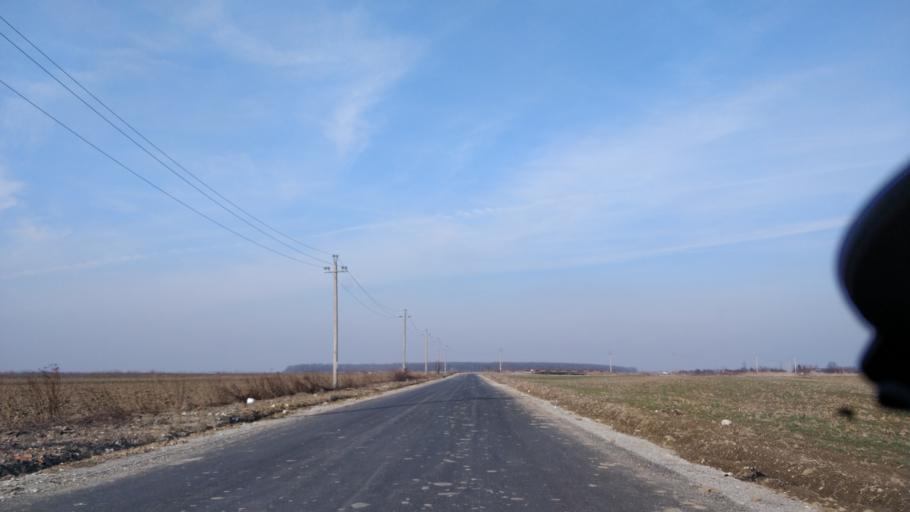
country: RO
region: Giurgiu
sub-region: Comuna Ulmi
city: Trestieni
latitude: 44.5148
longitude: 25.7669
